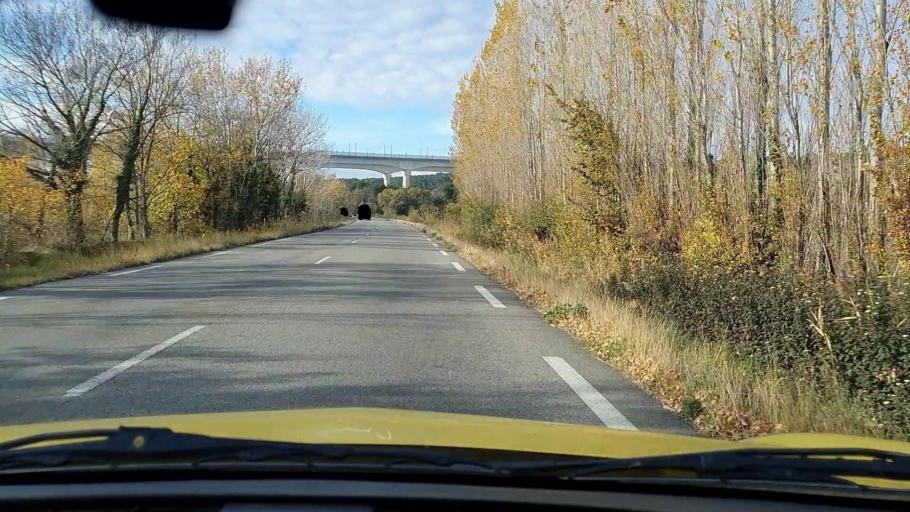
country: FR
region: Languedoc-Roussillon
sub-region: Departement du Gard
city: Les Angles
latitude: 43.9384
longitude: 4.7606
